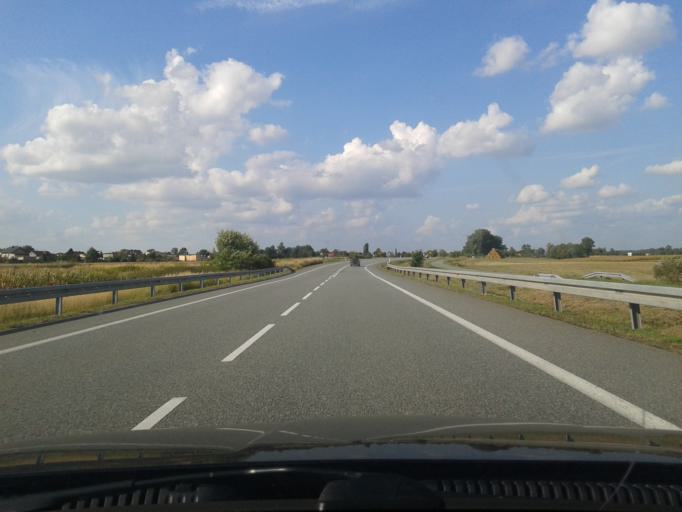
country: PL
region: Silesian Voivodeship
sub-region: Powiat raciborski
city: Chalupki
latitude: 49.9273
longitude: 18.3244
